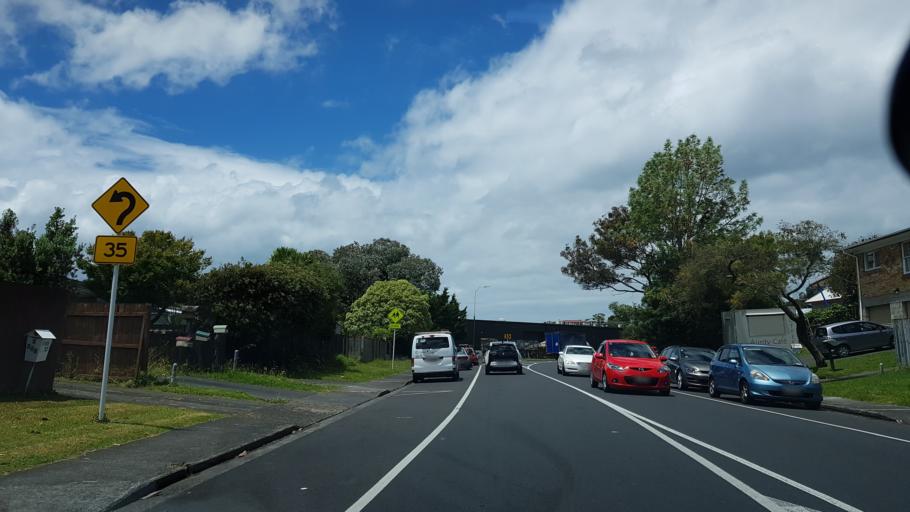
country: NZ
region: Auckland
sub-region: Auckland
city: North Shore
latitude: -36.7772
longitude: 174.7323
